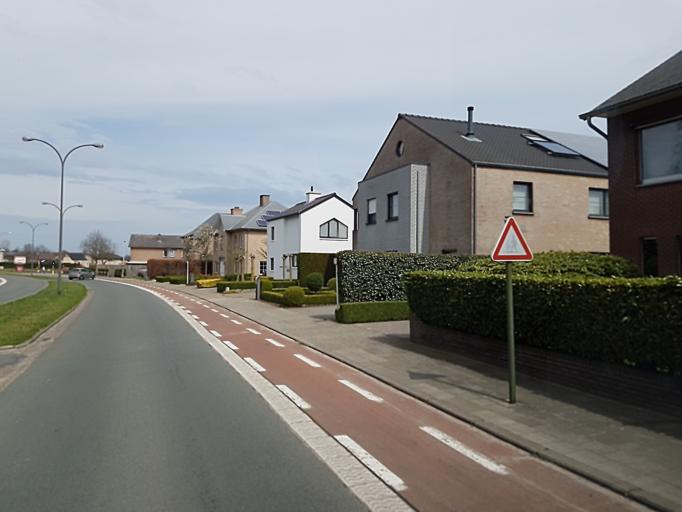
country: BE
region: Flanders
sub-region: Provincie Limburg
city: Overpelt
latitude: 51.2119
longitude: 5.4325
